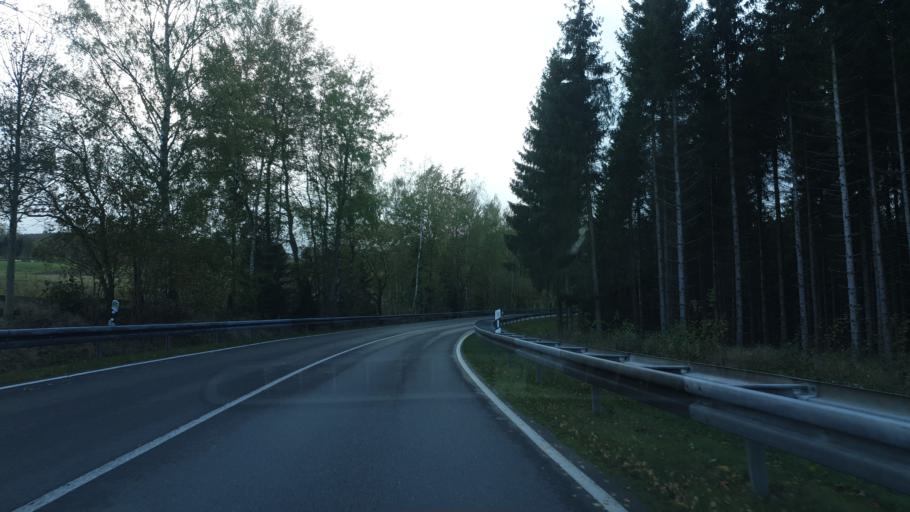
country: DE
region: Saxony
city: Eibenstock
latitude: 50.5057
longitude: 12.5906
